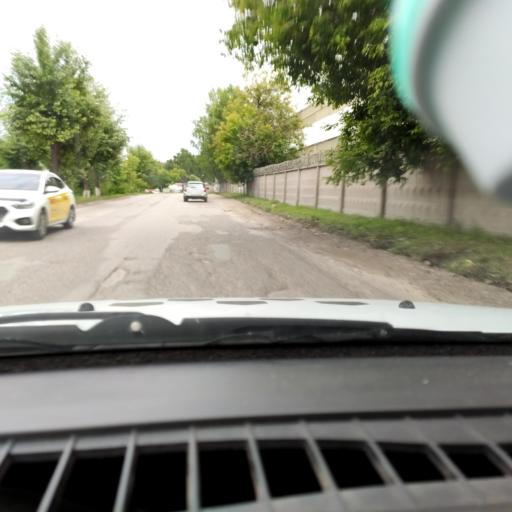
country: RU
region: Perm
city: Chusovoy
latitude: 58.2923
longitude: 57.8163
